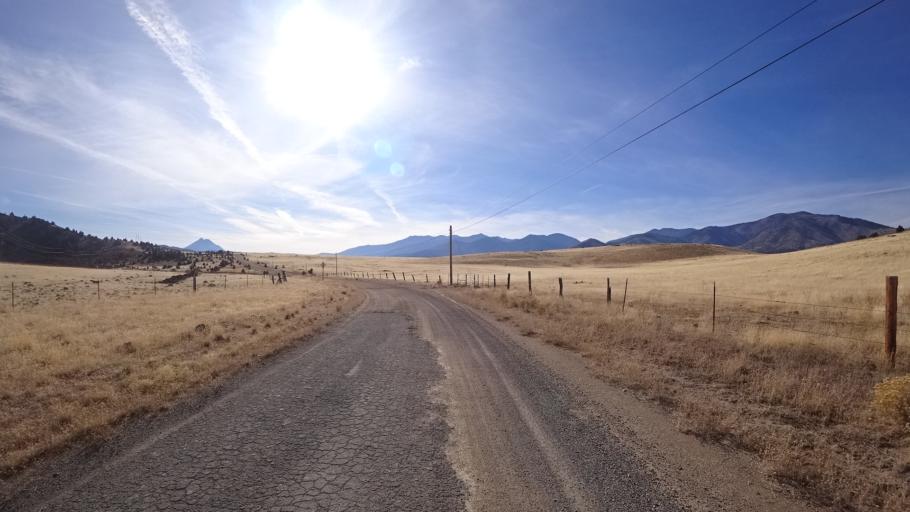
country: US
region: California
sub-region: Siskiyou County
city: Weed
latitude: 41.4968
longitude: -122.4553
